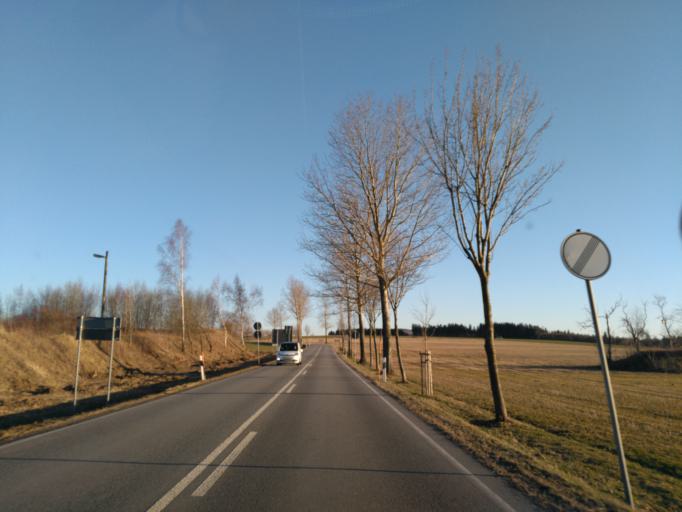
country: DE
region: Saxony
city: Konigswalde
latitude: 50.5481
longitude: 13.0183
